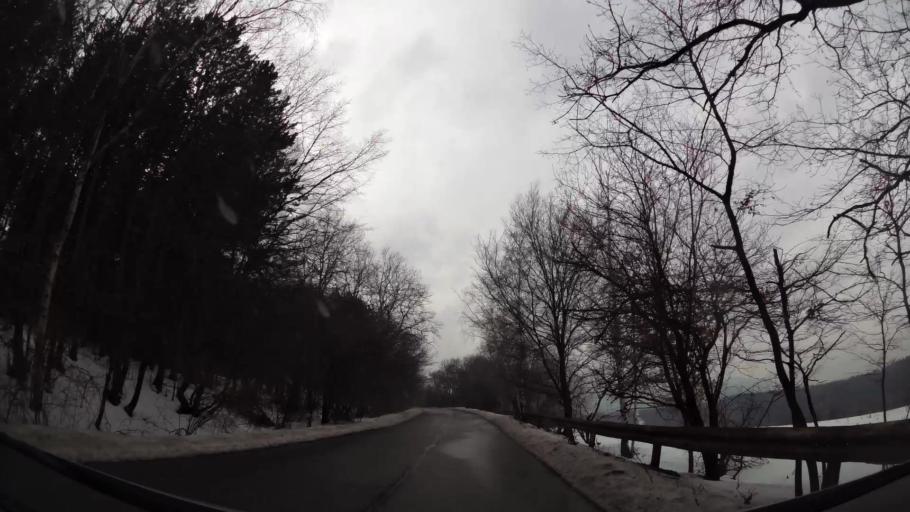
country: BG
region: Sofiya
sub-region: Obshtina Bozhurishte
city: Bozhurishte
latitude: 42.6595
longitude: 23.2062
